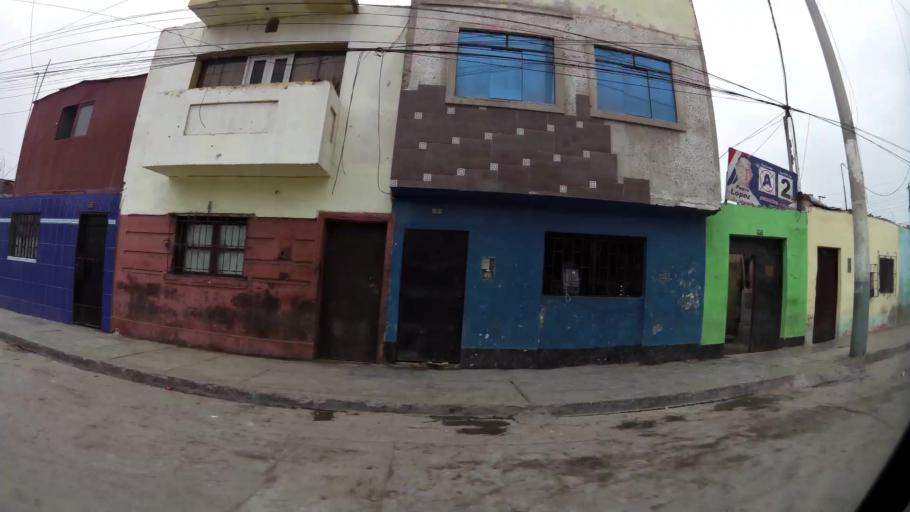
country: PE
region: Callao
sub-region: Callao
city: Callao
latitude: -12.0658
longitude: -77.1422
